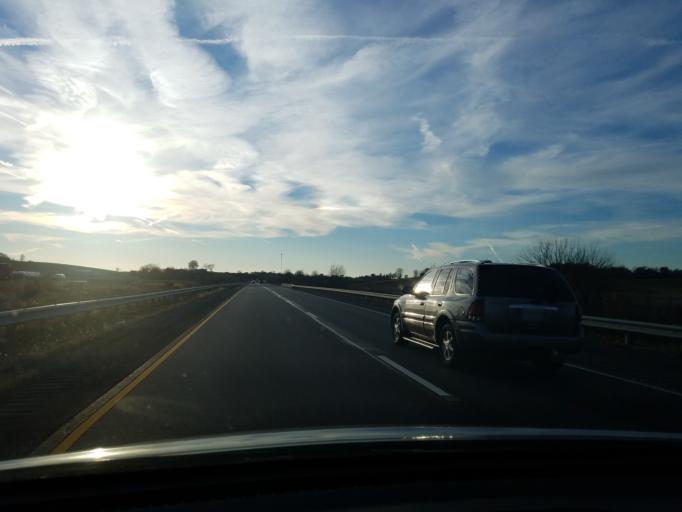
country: US
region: Indiana
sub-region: Dubois County
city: Ferdinand
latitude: 38.2021
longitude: -86.9073
